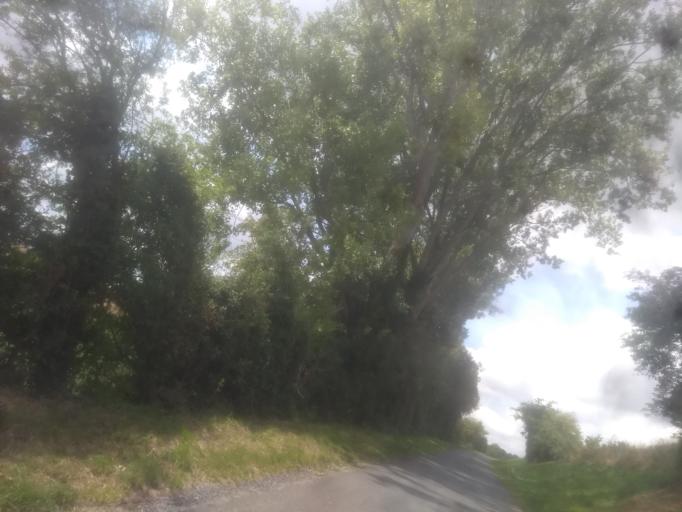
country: FR
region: Nord-Pas-de-Calais
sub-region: Departement du Pas-de-Calais
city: Beaumetz-les-Loges
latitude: 50.2264
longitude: 2.6569
